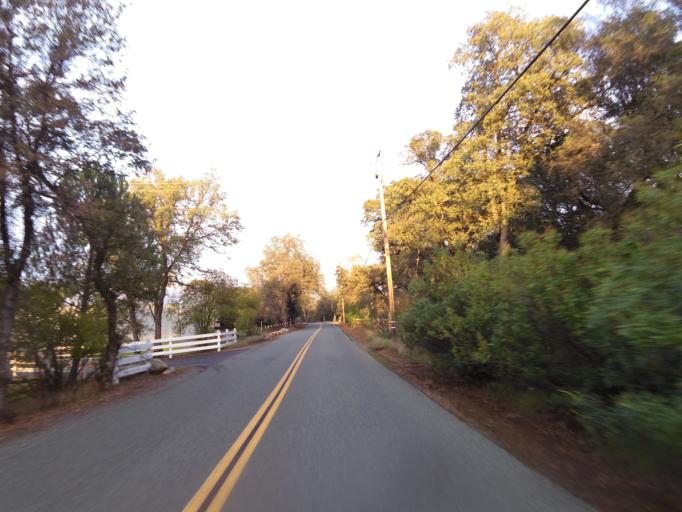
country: US
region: California
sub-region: El Dorado County
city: Cameron Park
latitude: 38.7353
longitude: -121.0000
